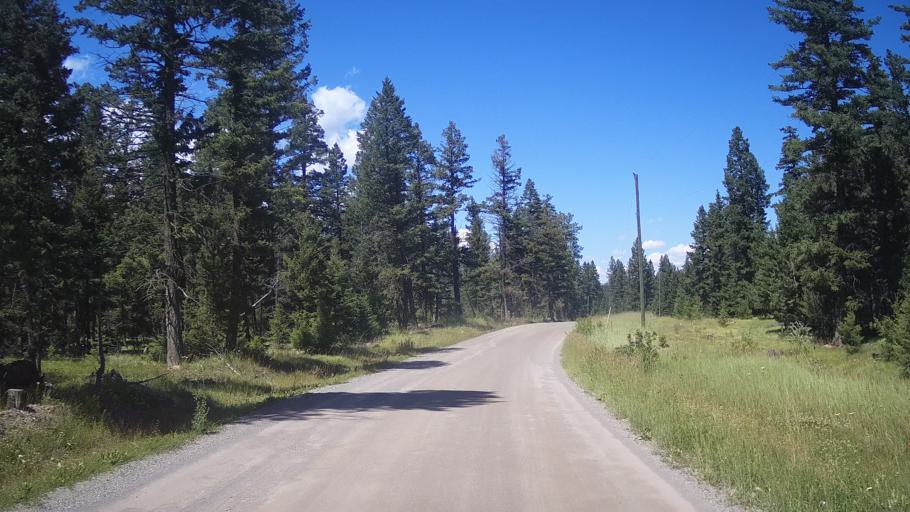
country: CA
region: British Columbia
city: Cache Creek
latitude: 51.2129
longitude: -121.6026
